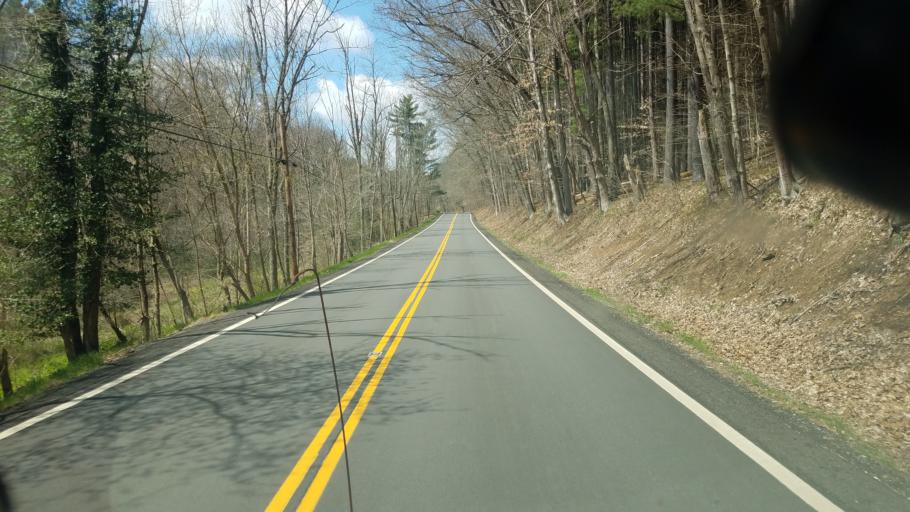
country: US
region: Ohio
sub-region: Ashland County
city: Loudonville
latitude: 40.5997
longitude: -82.2886
